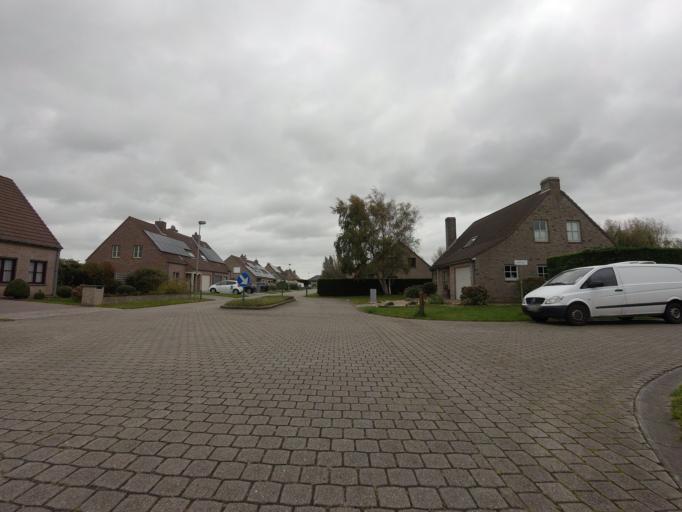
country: BE
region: Flanders
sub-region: Provincie West-Vlaanderen
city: Bredene
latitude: 51.2337
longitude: 2.9661
